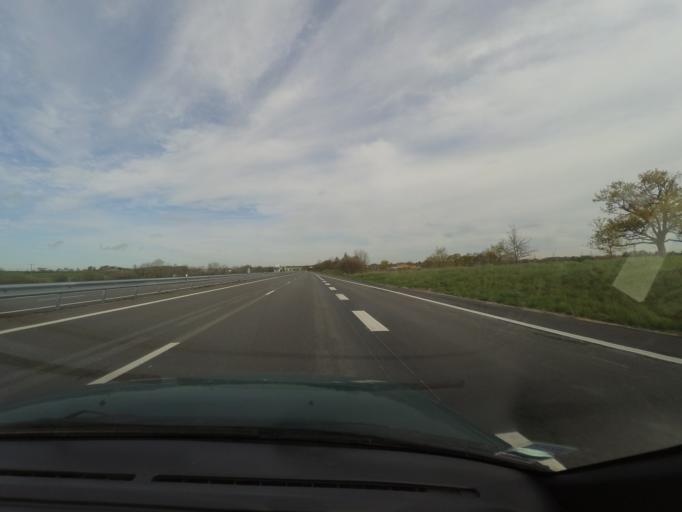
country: FR
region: Pays de la Loire
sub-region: Departement de la Loire-Atlantique
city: Aigrefeuille-sur-Maine
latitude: 47.0741
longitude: -1.4390
